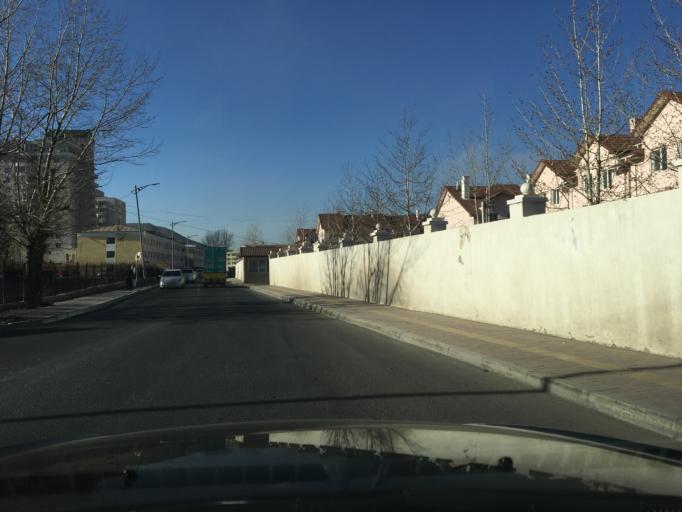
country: MN
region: Ulaanbaatar
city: Ulaanbaatar
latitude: 47.8876
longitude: 106.9095
